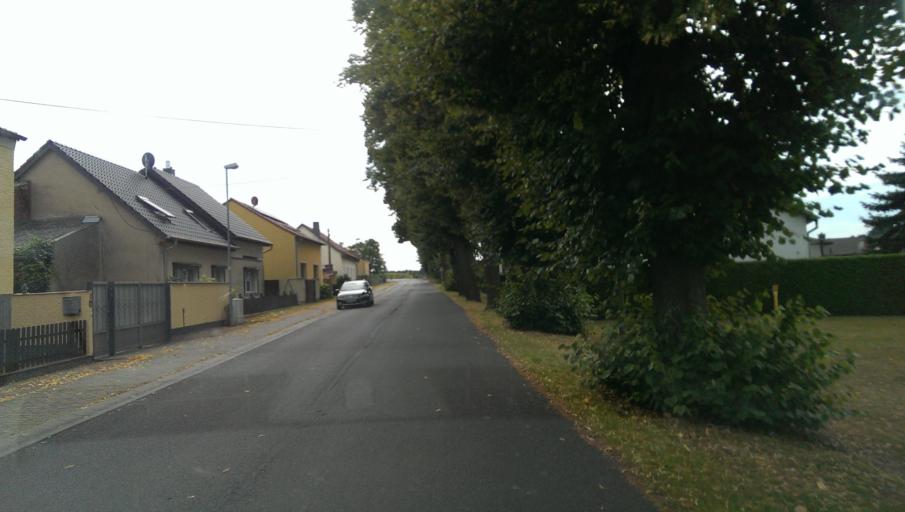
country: DE
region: Brandenburg
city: Trebbin
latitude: 52.1997
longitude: 13.2094
